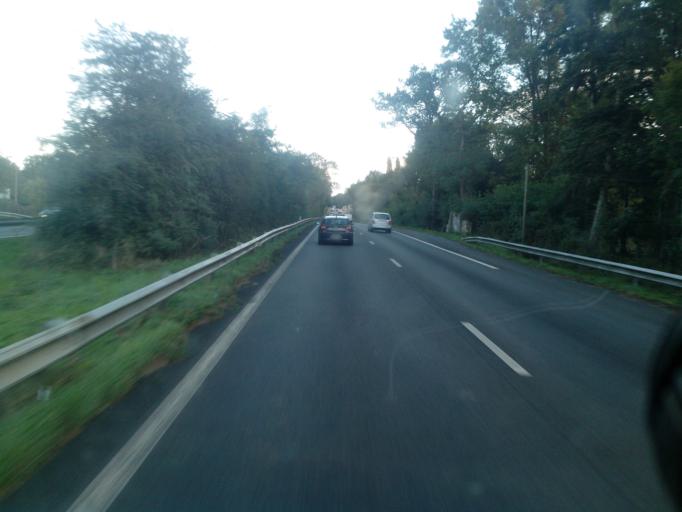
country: FR
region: Pays de la Loire
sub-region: Departement de la Loire-Atlantique
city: Vigneux-de-Bretagne
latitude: 47.2882
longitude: -1.7372
